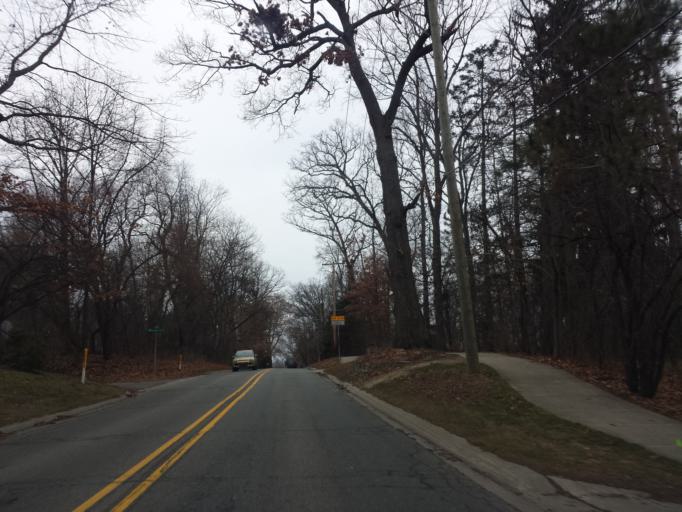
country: US
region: Michigan
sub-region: Oakland County
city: Bloomfield Hills
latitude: 42.5962
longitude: -83.2693
